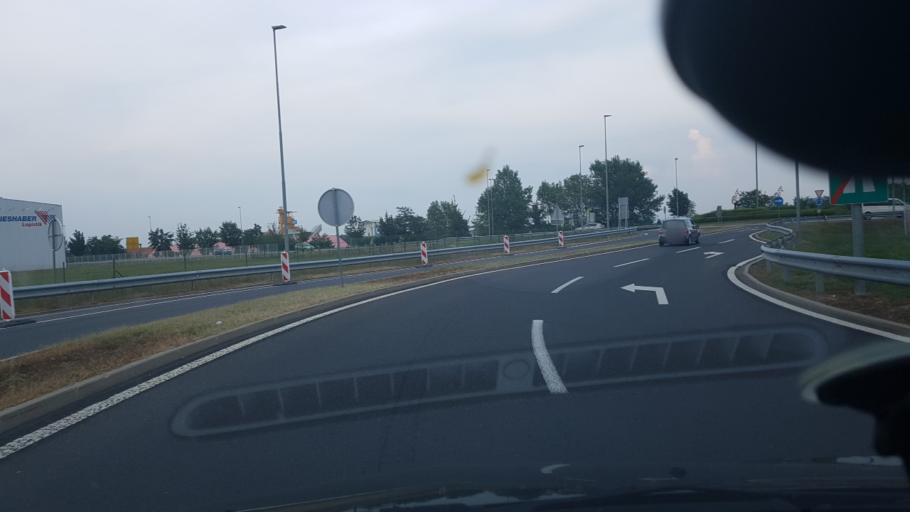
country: SI
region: Krsko
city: Leskovec pri Krskem
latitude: 45.9156
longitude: 15.4698
